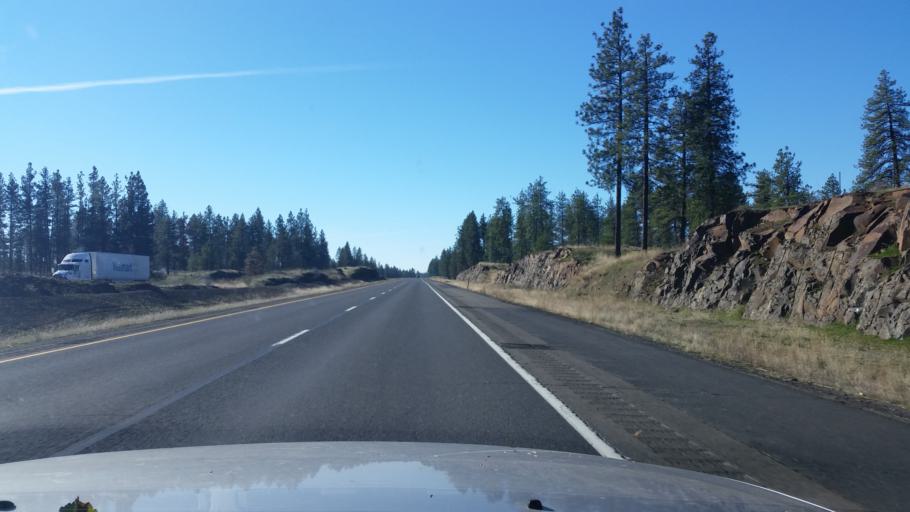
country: US
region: Washington
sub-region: Spokane County
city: Medical Lake
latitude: 47.5218
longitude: -117.6671
